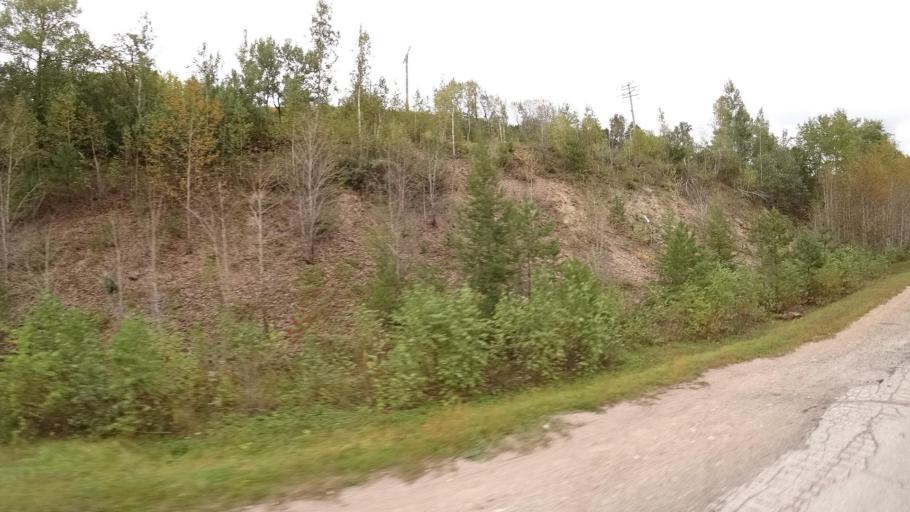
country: RU
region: Jewish Autonomous Oblast
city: Khingansk
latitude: 48.9883
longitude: 131.0634
